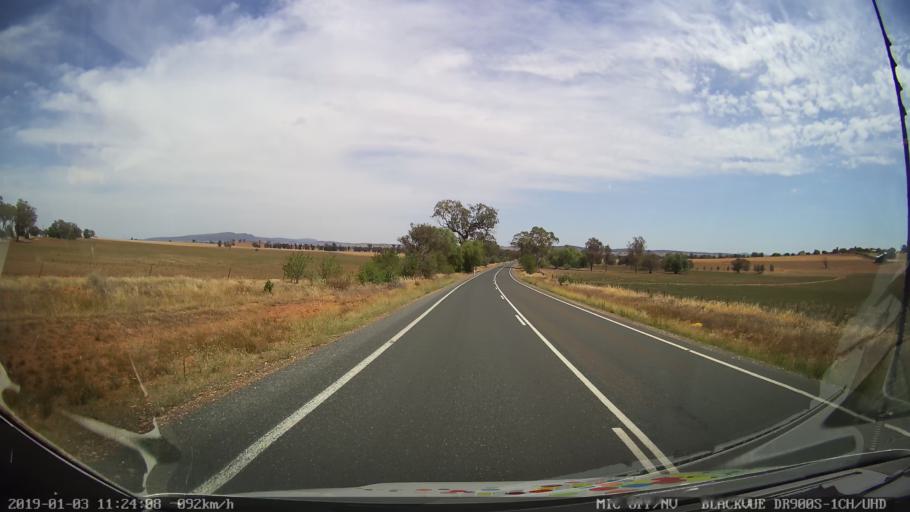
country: AU
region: New South Wales
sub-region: Weddin
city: Grenfell
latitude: -34.0552
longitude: 148.2372
